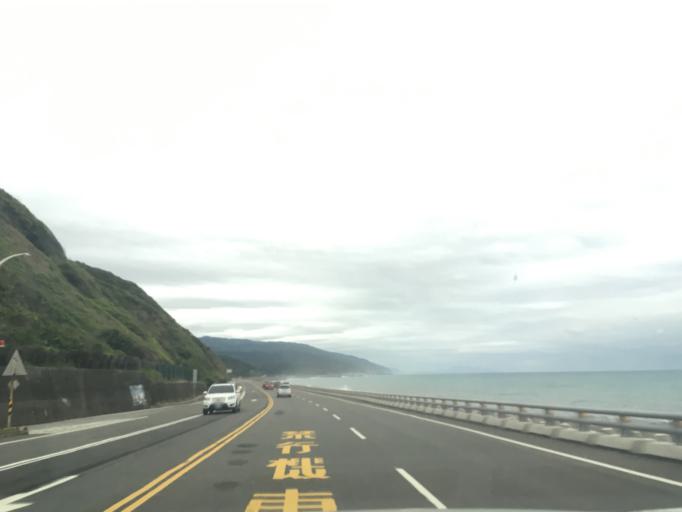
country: TW
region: Taiwan
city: Hengchun
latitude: 22.3106
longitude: 120.8910
